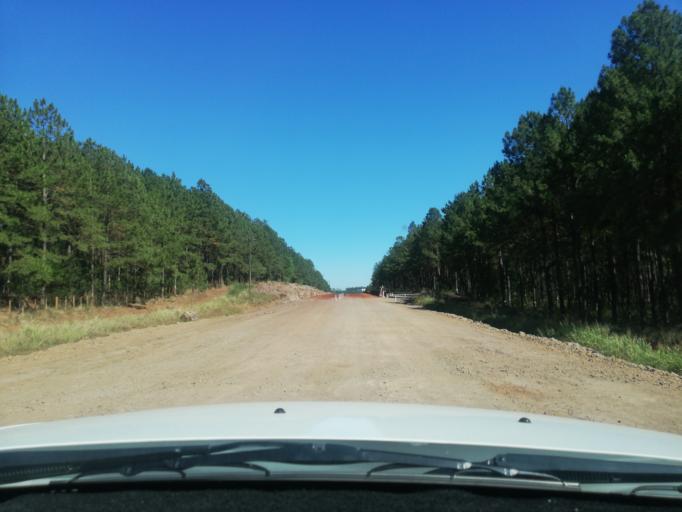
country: AR
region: Misiones
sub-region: Departamento de Candelaria
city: Candelaria
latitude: -27.5201
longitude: -55.7267
